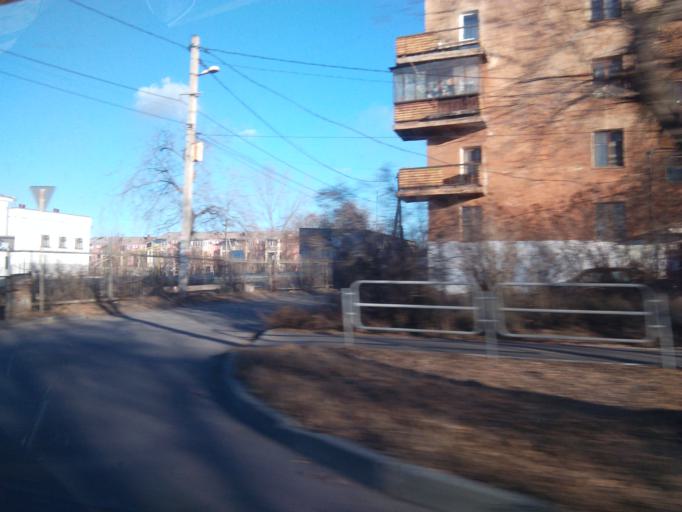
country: RU
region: Chelyabinsk
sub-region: Gorod Magnitogorsk
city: Magnitogorsk
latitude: 53.3907
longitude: 59.0521
